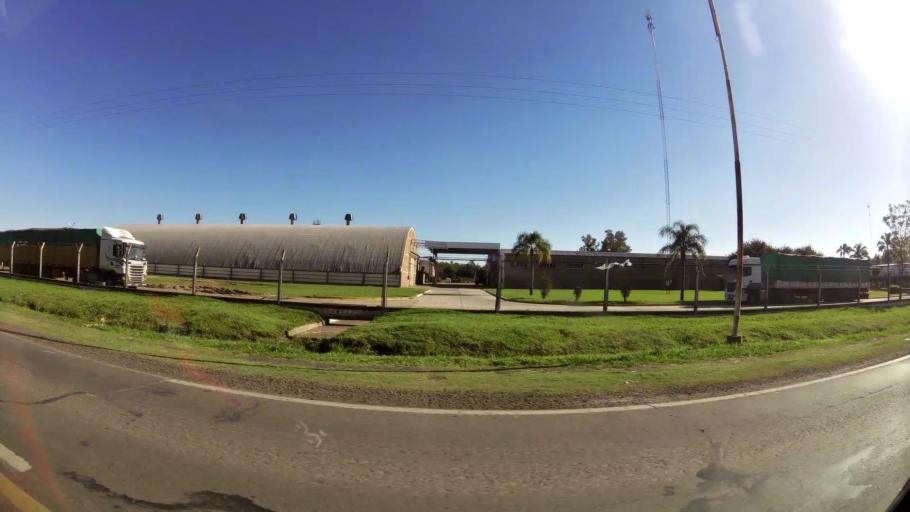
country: AR
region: Cordoba
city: San Francisco
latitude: -31.4244
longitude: -62.0517
